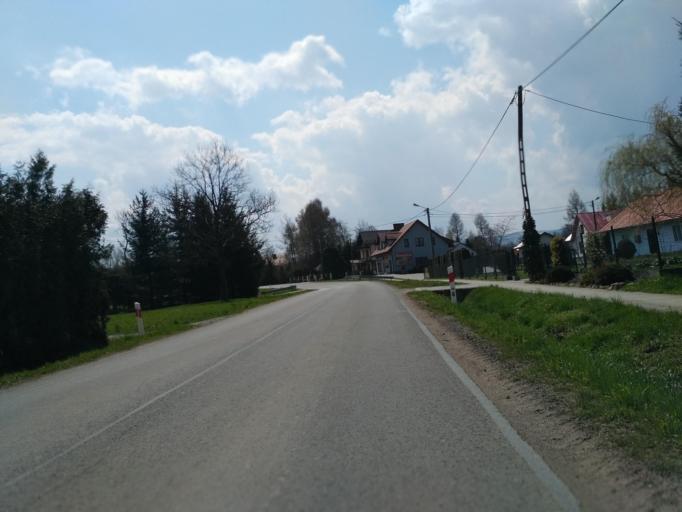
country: PL
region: Subcarpathian Voivodeship
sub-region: Powiat sanocki
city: Bukowsko
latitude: 49.5043
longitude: 22.0328
